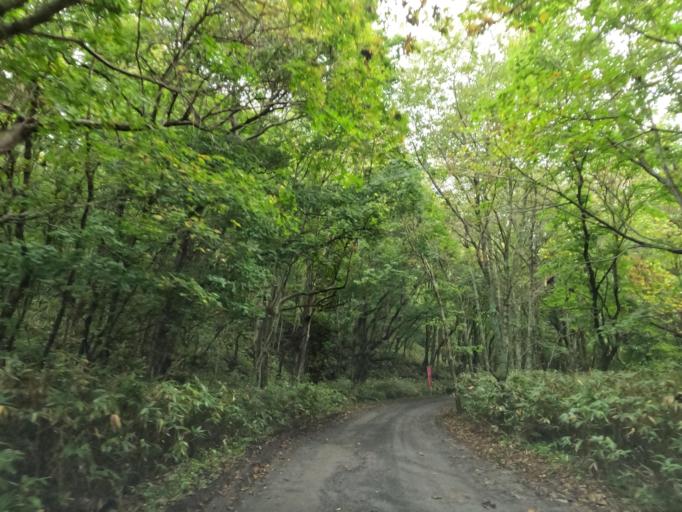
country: JP
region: Hokkaido
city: Date
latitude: 42.4999
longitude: 140.9245
